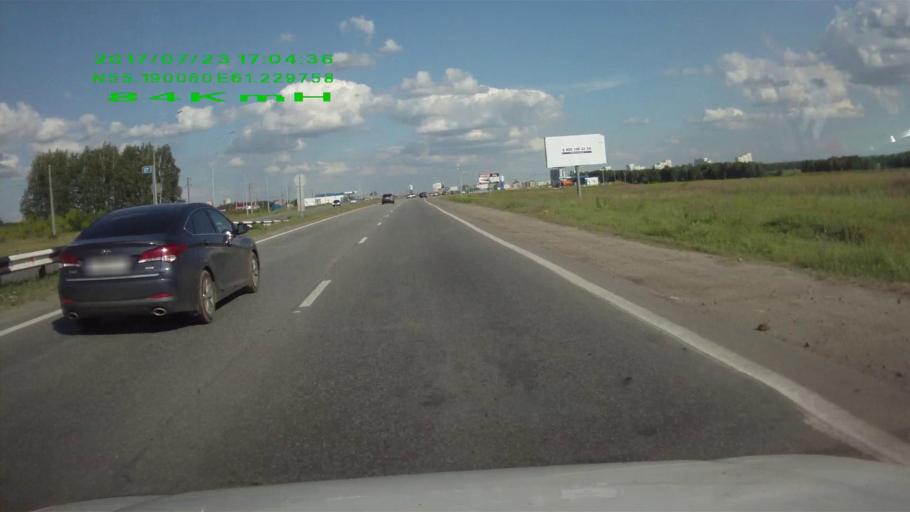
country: RU
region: Chelyabinsk
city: Roshchino
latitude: 55.1897
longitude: 61.2312
